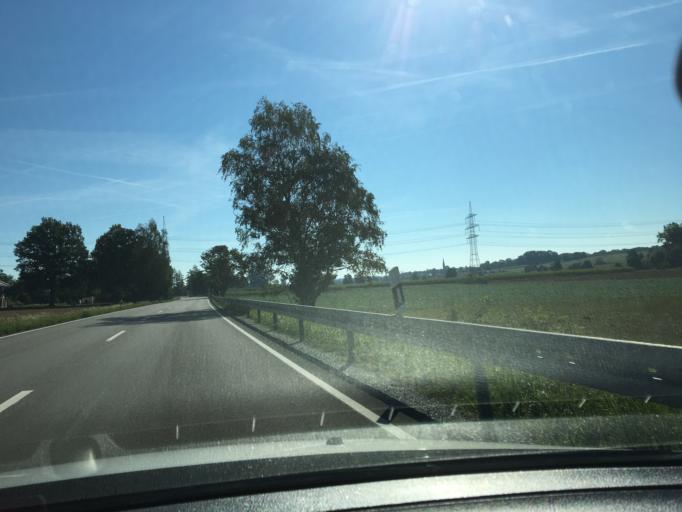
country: DE
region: Bavaria
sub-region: Upper Bavaria
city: Aham
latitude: 48.3467
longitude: 12.1477
